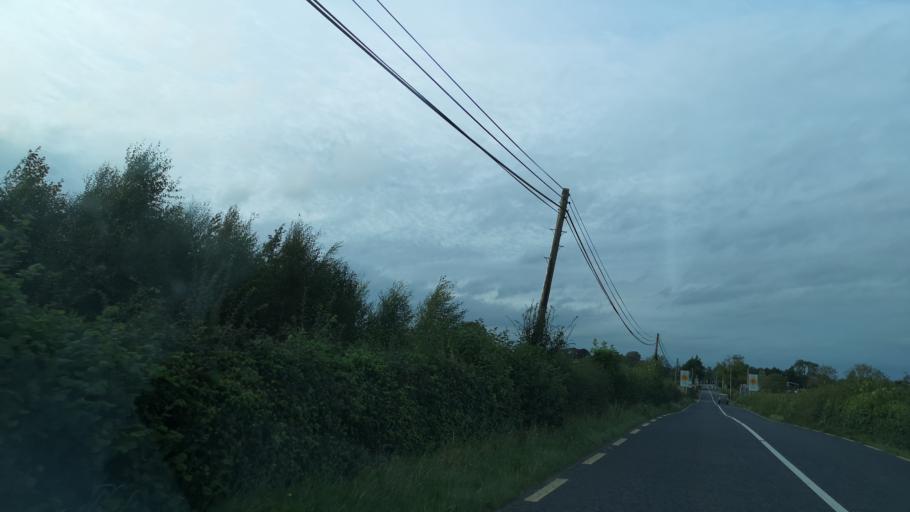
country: IE
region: Leinster
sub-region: Uibh Fhaili
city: Ferbane
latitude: 53.3286
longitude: -7.8220
